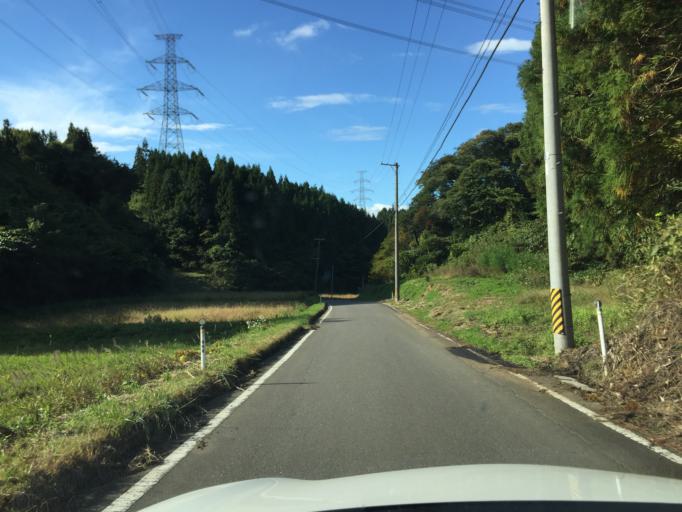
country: JP
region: Fukushima
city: Ishikawa
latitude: 37.1383
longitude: 140.5434
